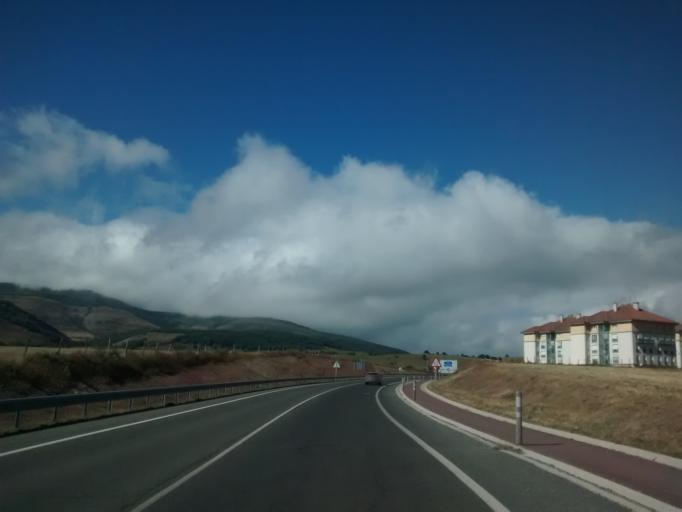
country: ES
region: Cantabria
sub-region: Provincia de Cantabria
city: Reinosa
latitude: 43.0051
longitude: -4.1420
